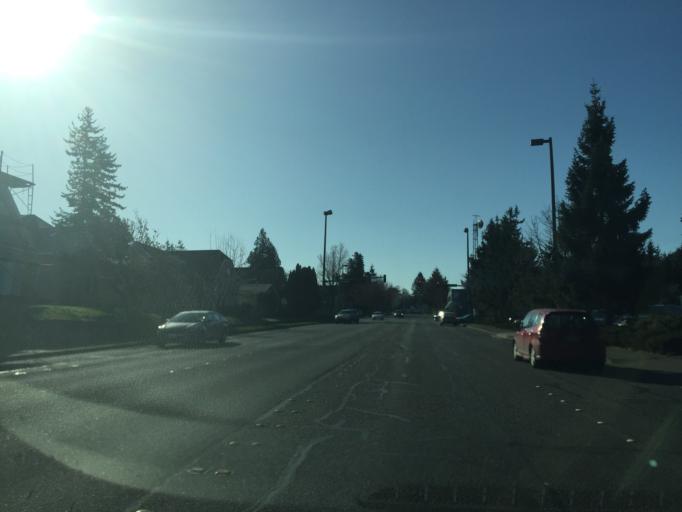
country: US
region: Washington
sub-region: Whatcom County
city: Bellingham
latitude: 48.7442
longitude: -122.4718
